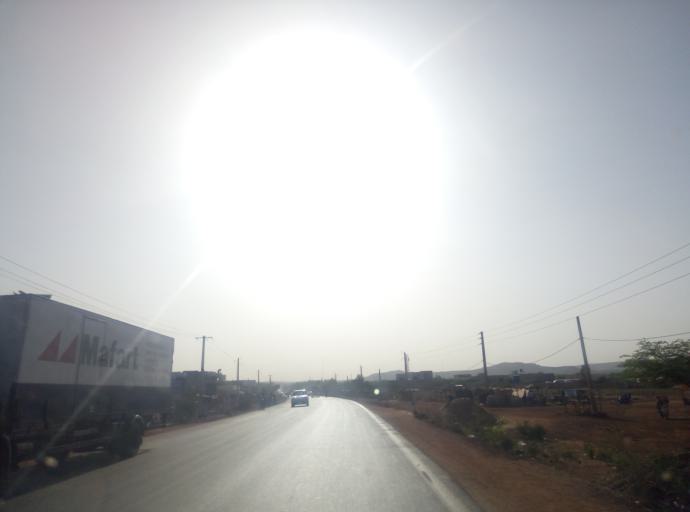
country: ML
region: Bamako
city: Bamako
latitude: 12.5869
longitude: -7.8312
